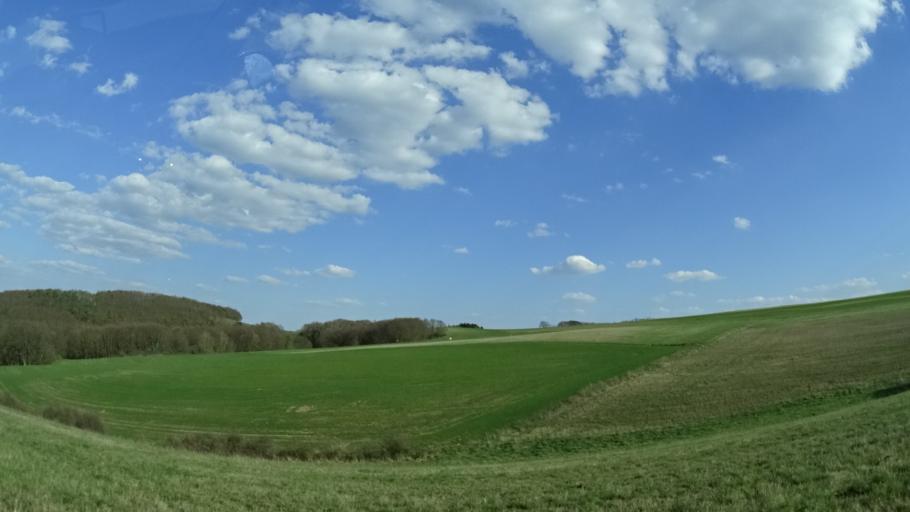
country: DE
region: Rheinland-Pfalz
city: Kirschroth
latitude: 49.7481
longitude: 7.5668
